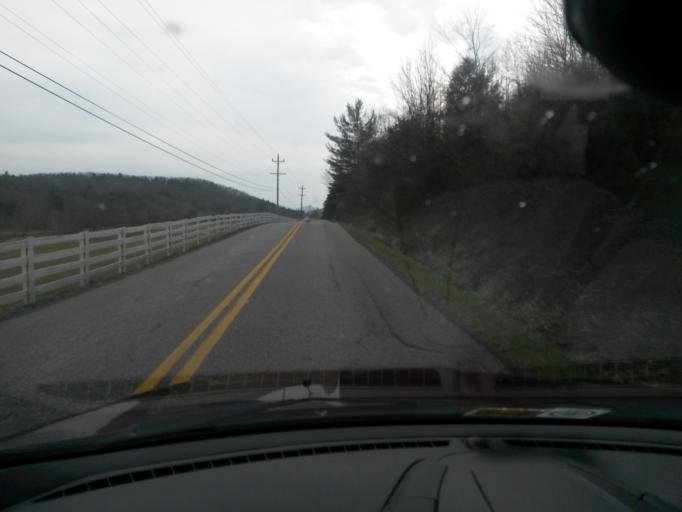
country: US
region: Virginia
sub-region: Bath County
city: Warm Springs
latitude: 37.9903
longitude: -79.8965
